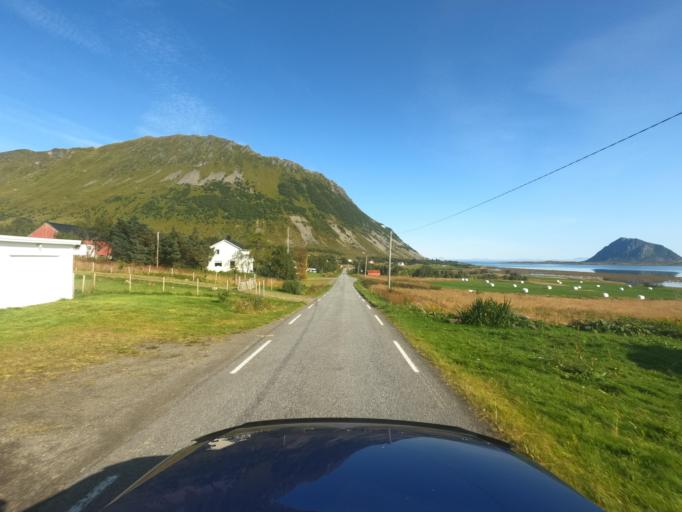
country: NO
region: Nordland
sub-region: Vestvagoy
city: Evjen
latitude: 68.2939
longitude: 14.0016
